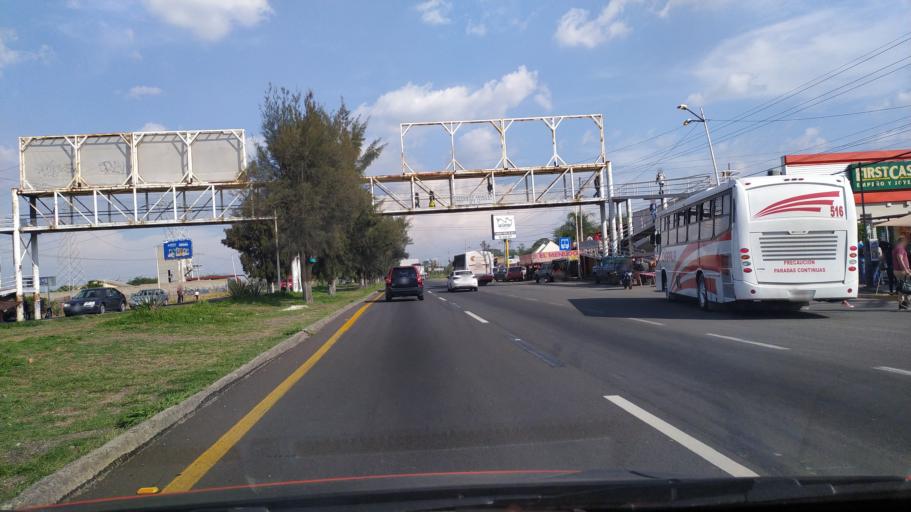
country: MX
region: Jalisco
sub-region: Tlajomulco de Zuniga
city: Rancho Alegre [Fraccionamiento]
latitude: 20.4767
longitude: -103.2650
